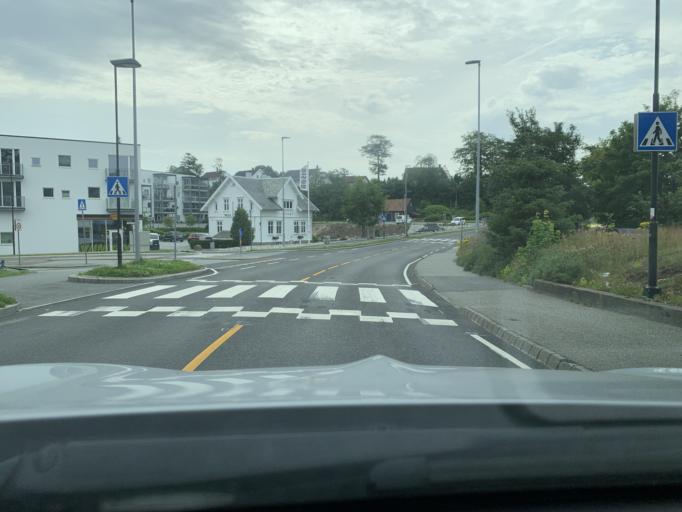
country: NO
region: Rogaland
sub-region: Sandnes
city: Sandnes
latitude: 58.7791
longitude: 5.7206
